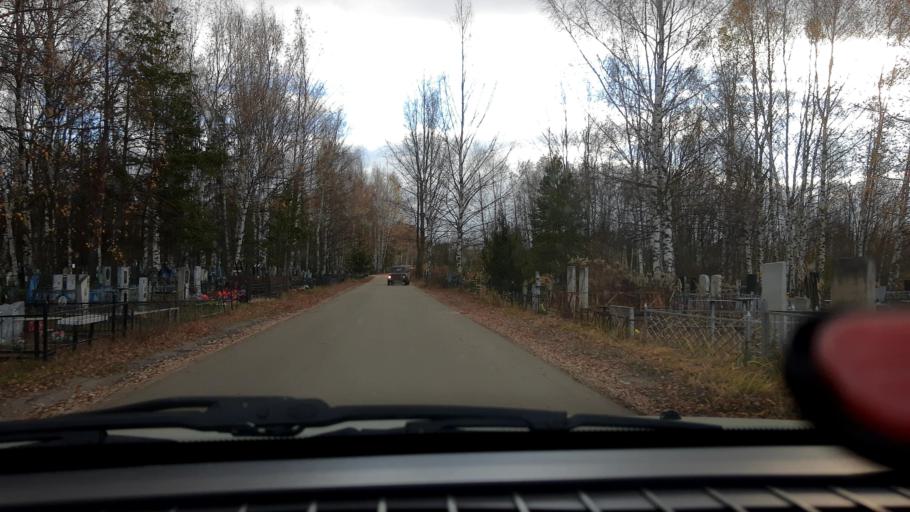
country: RU
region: Nizjnij Novgorod
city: Gorbatovka
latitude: 56.3578
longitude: 43.7775
